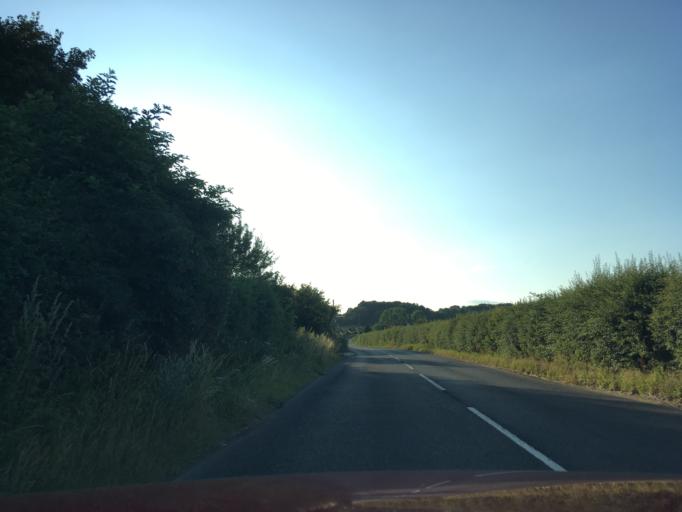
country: GB
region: England
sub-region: West Berkshire
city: Theale
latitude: 51.4108
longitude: -1.1310
